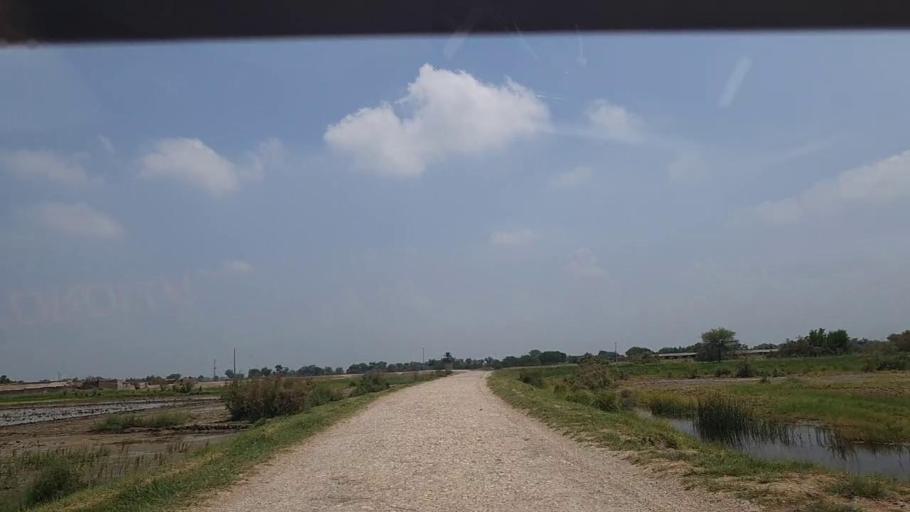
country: PK
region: Sindh
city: Khanpur
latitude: 27.8940
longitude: 69.3980
